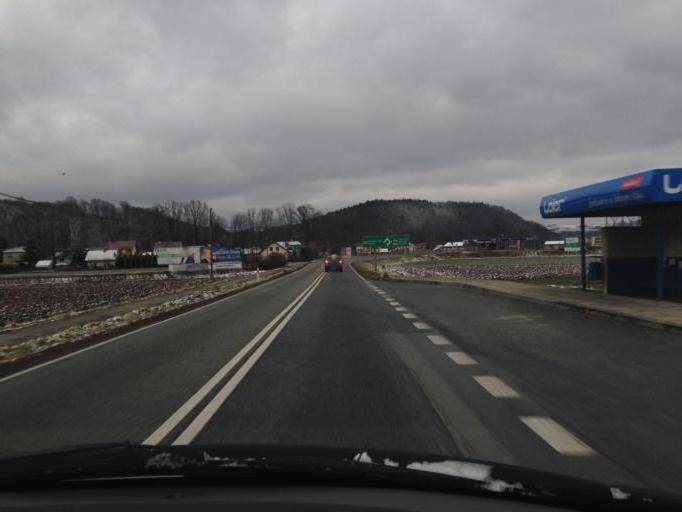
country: PL
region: Lesser Poland Voivodeship
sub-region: Powiat tarnowski
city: Zakliczyn
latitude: 49.8713
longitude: 20.8079
